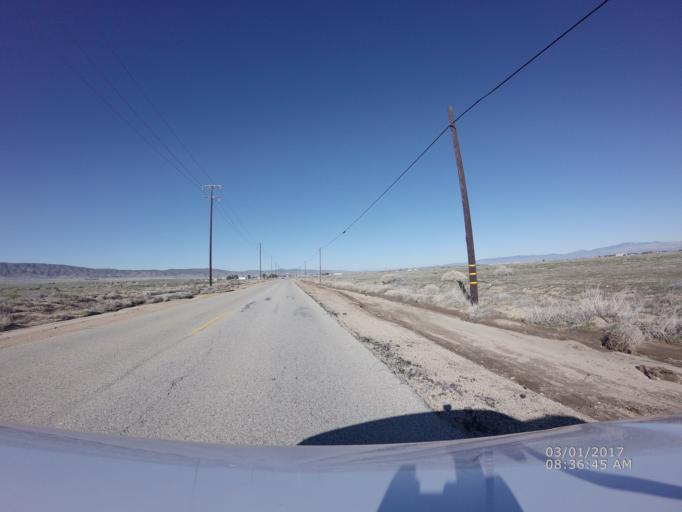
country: US
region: California
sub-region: Los Angeles County
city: Quartz Hill
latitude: 34.6894
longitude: -118.2695
